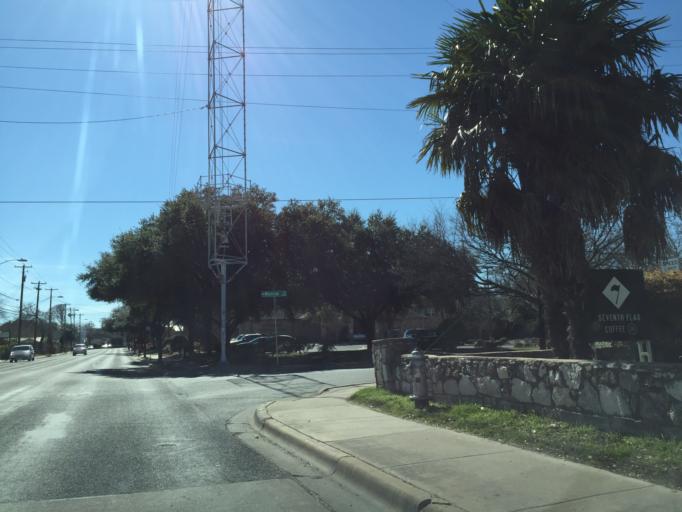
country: US
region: Texas
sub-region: Travis County
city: Austin
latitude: 30.2497
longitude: -97.7551
